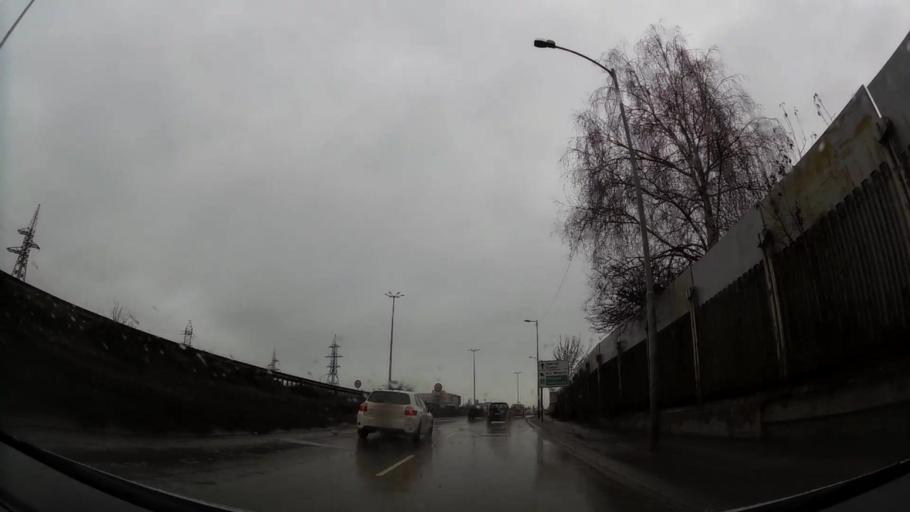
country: BG
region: Sofia-Capital
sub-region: Stolichna Obshtina
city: Sofia
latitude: 42.6605
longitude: 23.3889
